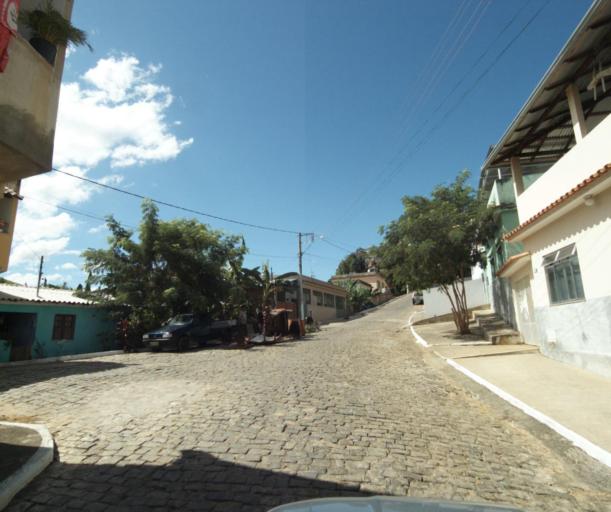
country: BR
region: Espirito Santo
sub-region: Sao Jose Do Calcado
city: Sao Jose do Calcado
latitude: -21.0252
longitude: -41.6576
